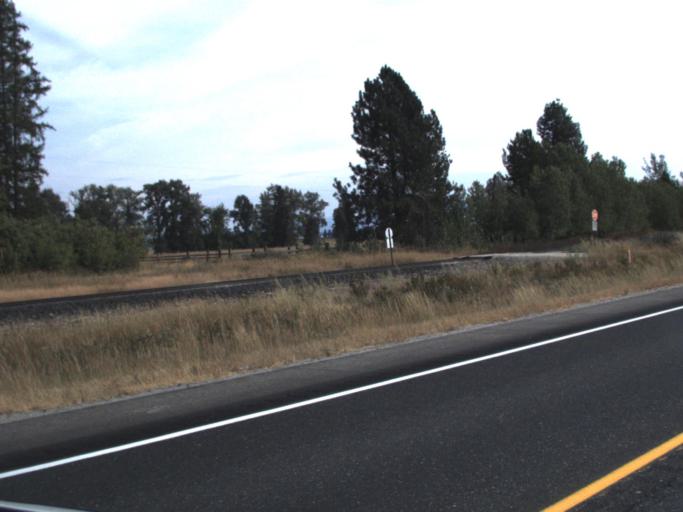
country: US
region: Washington
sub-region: Spokane County
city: Deer Park
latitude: 47.9921
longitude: -117.5436
